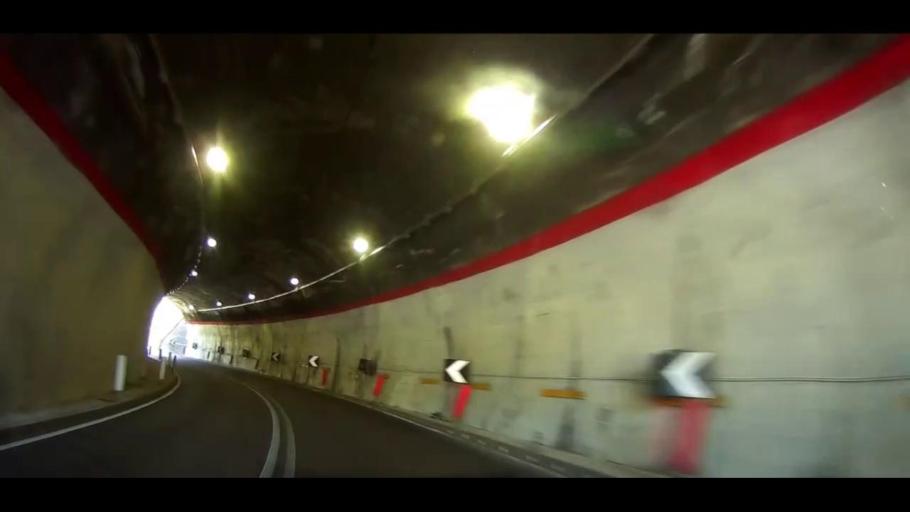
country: IT
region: Calabria
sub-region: Provincia di Cosenza
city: Celico
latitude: 39.3126
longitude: 16.3388
